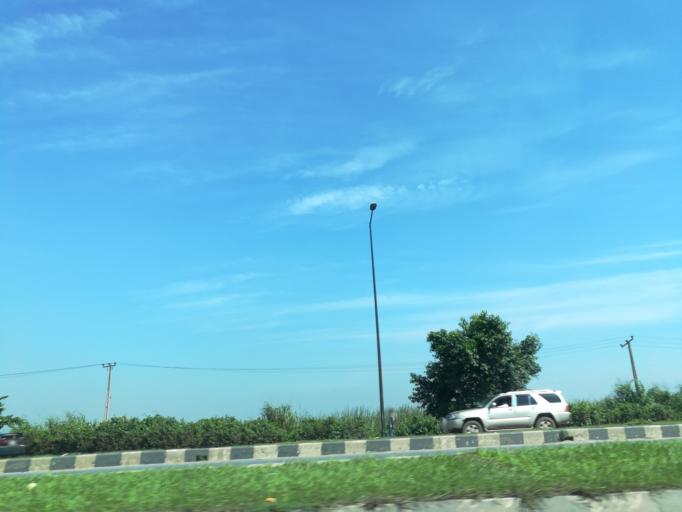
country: NG
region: Lagos
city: Ebute Ikorodu
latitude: 6.6195
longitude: 3.4496
